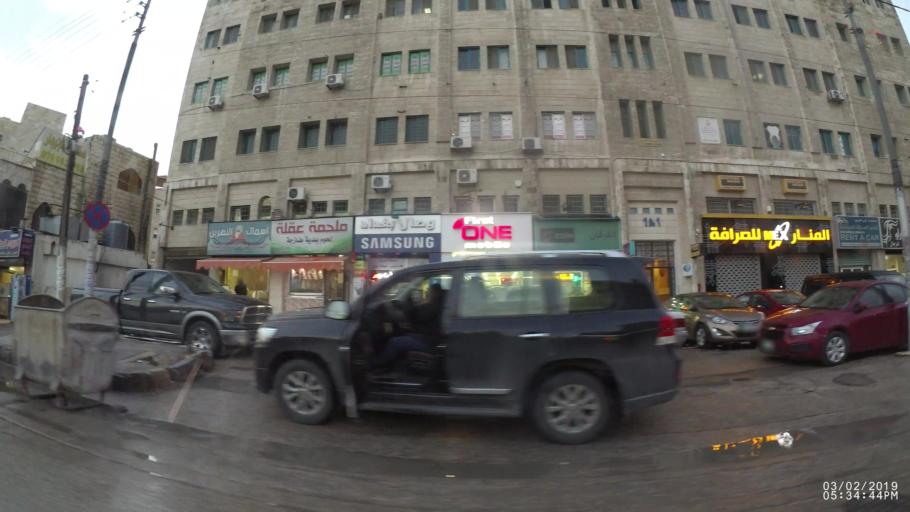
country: JO
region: Amman
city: Al Jubayhah
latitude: 31.9833
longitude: 35.8948
